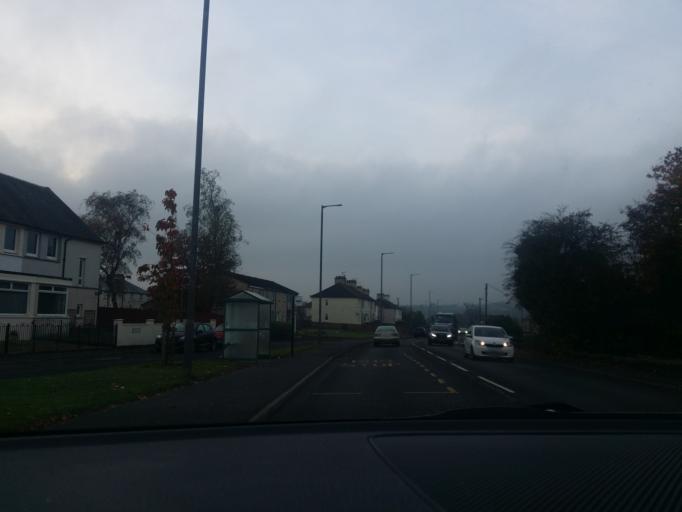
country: GB
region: Scotland
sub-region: Stirling
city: Bannockburn
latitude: 56.0913
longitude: -3.9324
